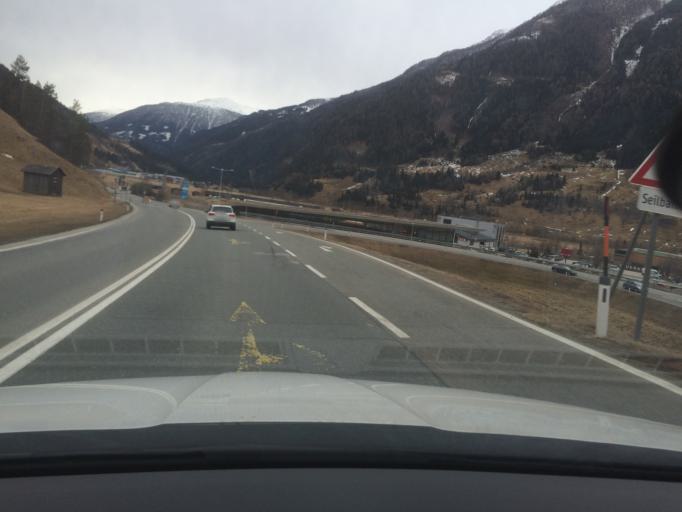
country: AT
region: Tyrol
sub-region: Politischer Bezirk Lienz
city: Matrei in Osttirol
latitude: 46.9926
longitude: 12.5432
